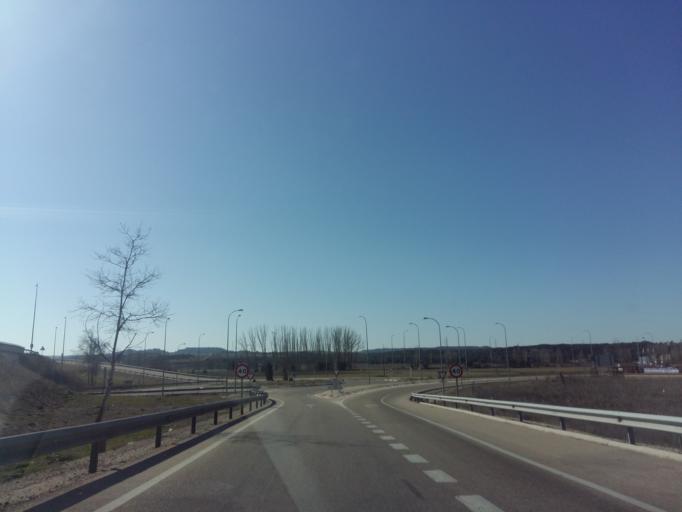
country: ES
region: Castille and Leon
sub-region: Provincia de Burgos
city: Villalba de Duero
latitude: 41.6654
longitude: -3.7289
